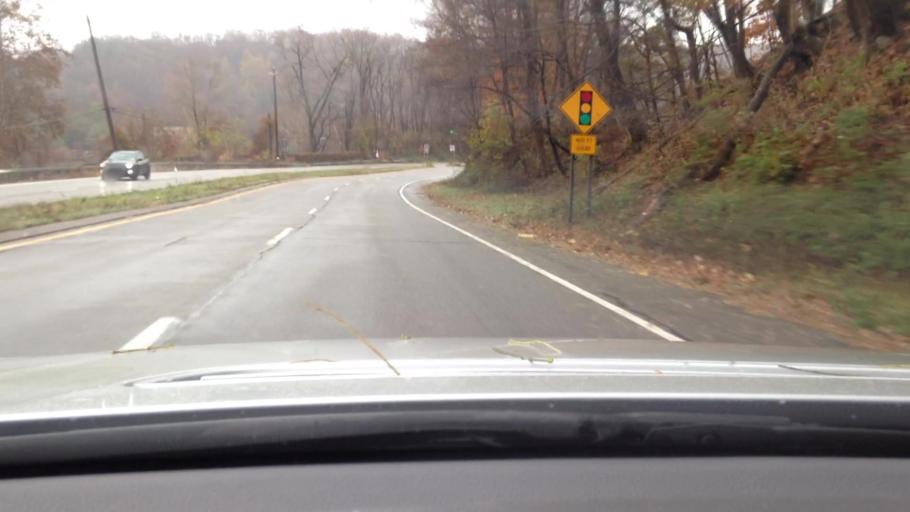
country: US
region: New York
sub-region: Westchester County
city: Peekskill
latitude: 41.3070
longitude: -73.9303
